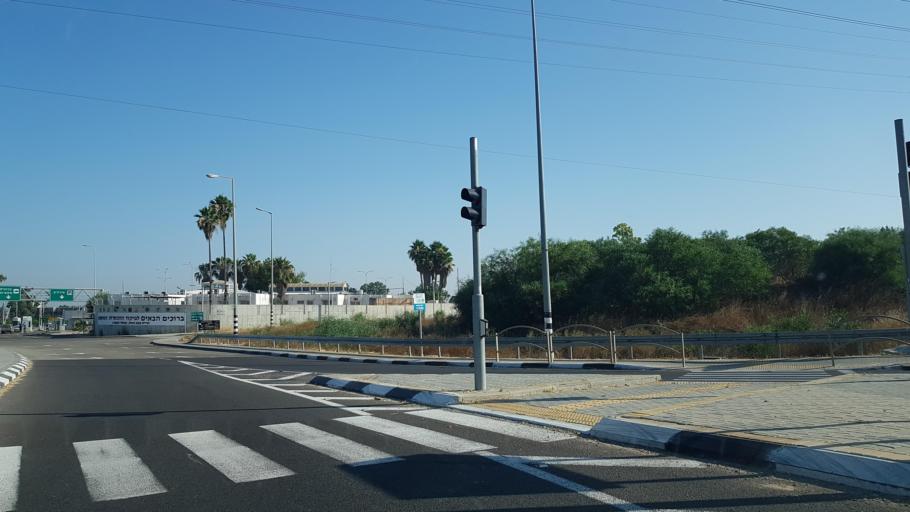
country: IL
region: Central District
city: Gan Yavne
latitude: 31.6909
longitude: 34.6789
